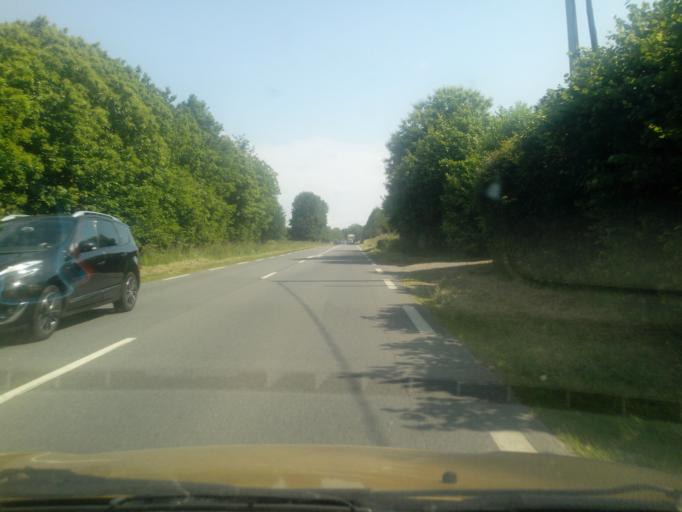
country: FR
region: Brittany
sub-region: Departement d'Ille-et-Vilaine
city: Melesse
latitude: 48.2022
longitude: -1.6943
